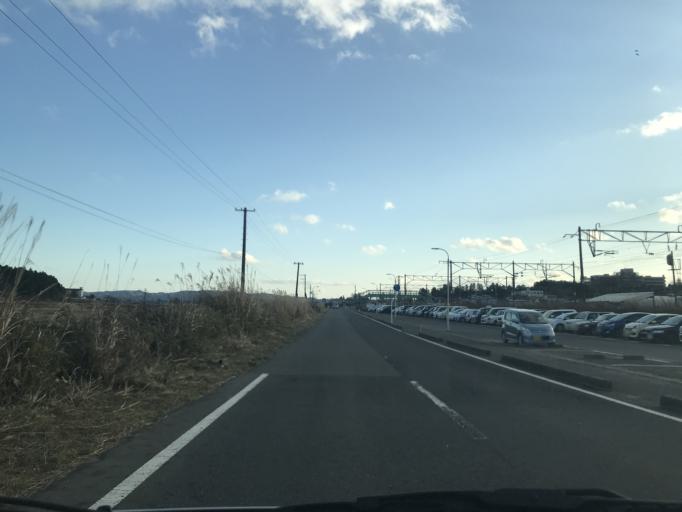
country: JP
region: Miyagi
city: Kogota
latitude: 38.6585
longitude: 141.0736
